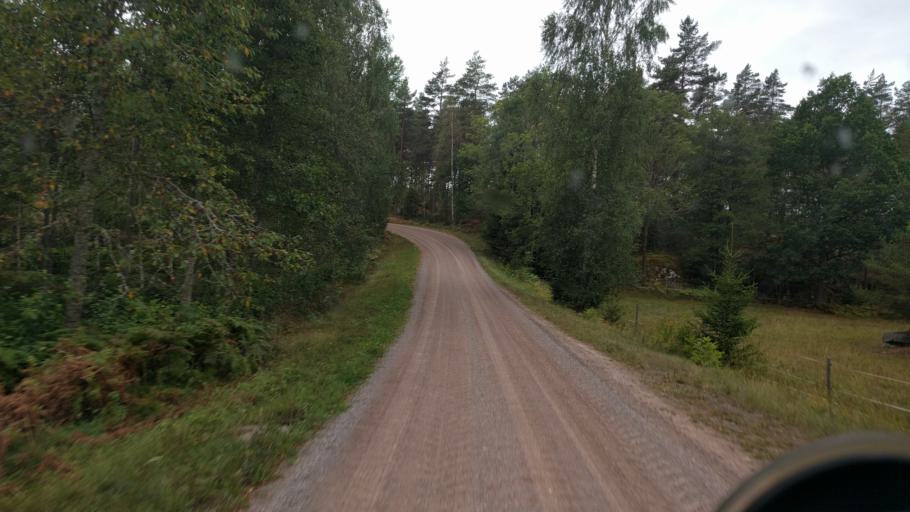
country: SE
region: Kalmar
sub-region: Vasterviks Kommun
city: Ankarsrum
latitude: 57.7835
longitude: 16.1969
